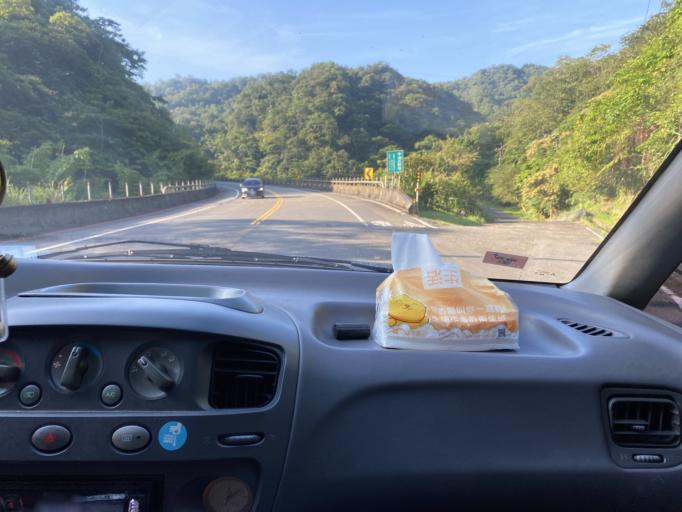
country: TW
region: Taiwan
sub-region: Keelung
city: Keelung
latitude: 25.0329
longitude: 121.7788
